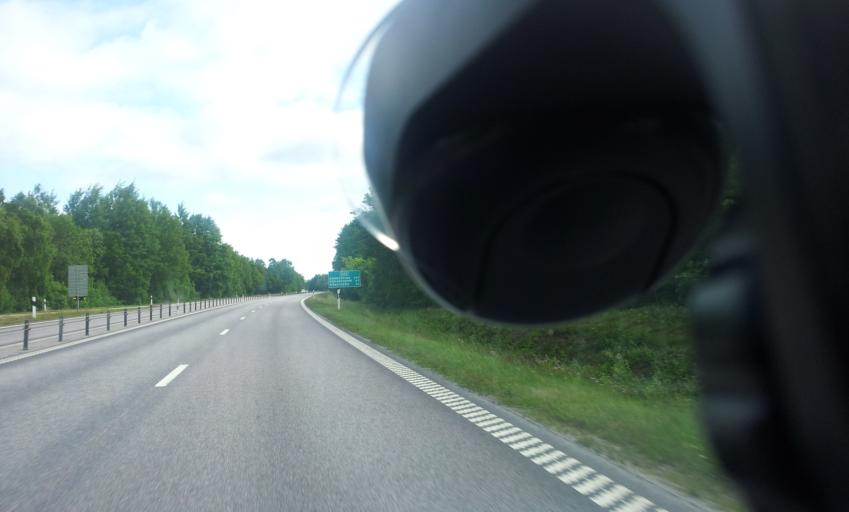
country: SE
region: Kalmar
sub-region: Kalmar Kommun
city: Lindsdal
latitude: 56.7599
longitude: 16.3113
